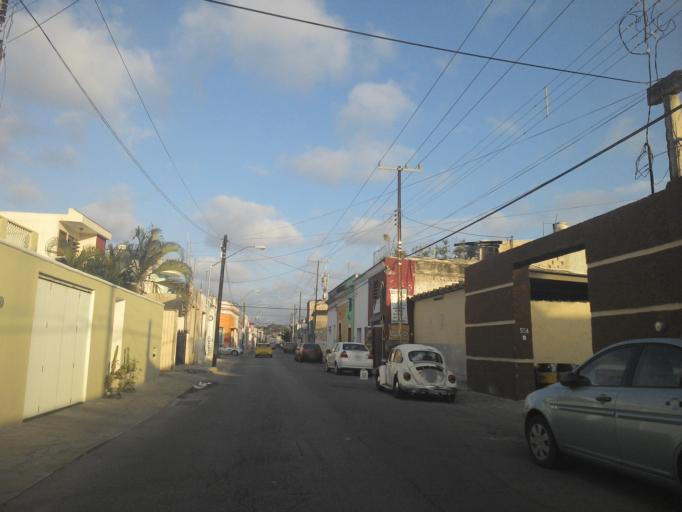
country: MX
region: Yucatan
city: Merida
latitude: 20.9764
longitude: -89.6274
